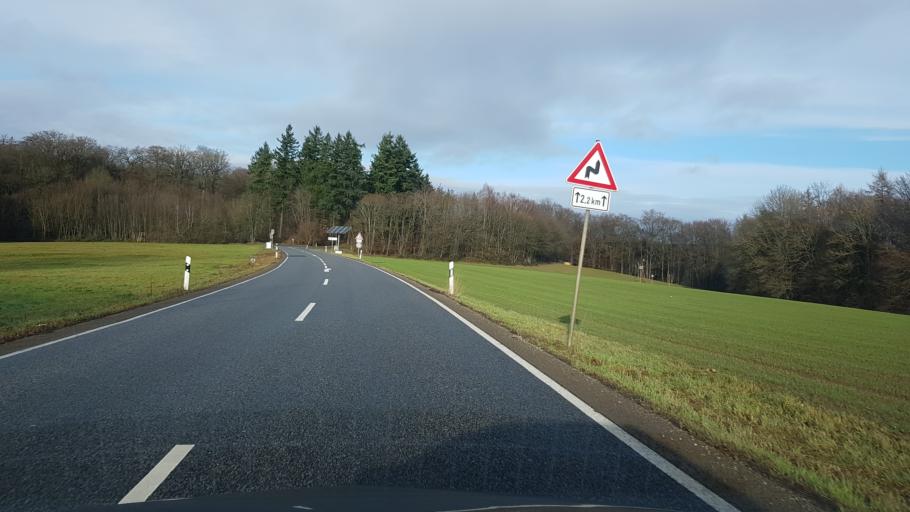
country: DE
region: Saarland
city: Sankt Ingbert
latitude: 49.2446
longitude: 7.1237
